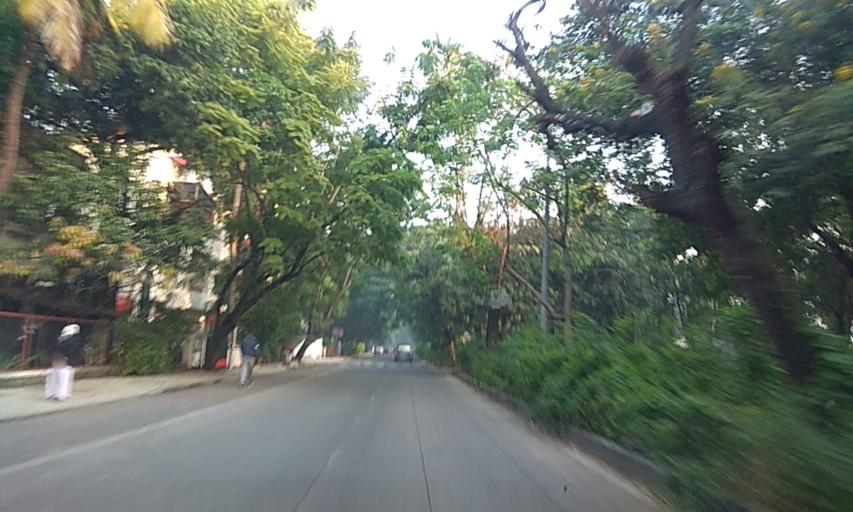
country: IN
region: Maharashtra
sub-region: Pune Division
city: Shivaji Nagar
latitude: 18.5422
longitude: 73.8174
